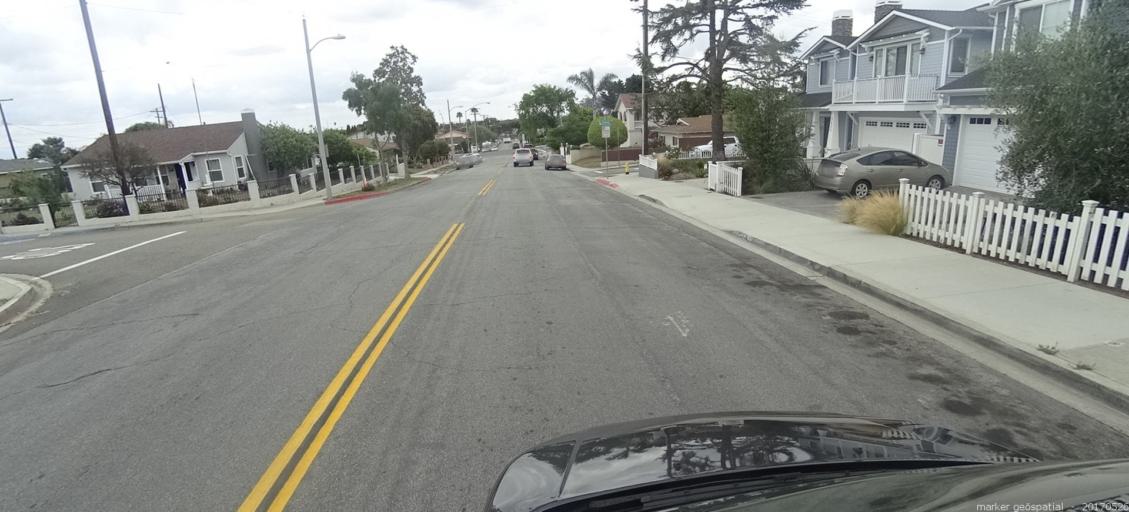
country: US
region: California
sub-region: Los Angeles County
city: Lawndale
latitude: 33.8801
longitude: -118.3627
